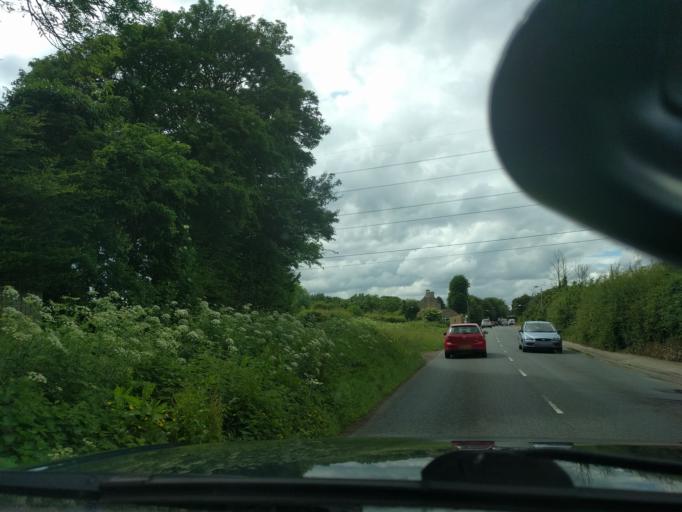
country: GB
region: England
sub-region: Wiltshire
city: Melksham
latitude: 51.3883
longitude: -2.1586
